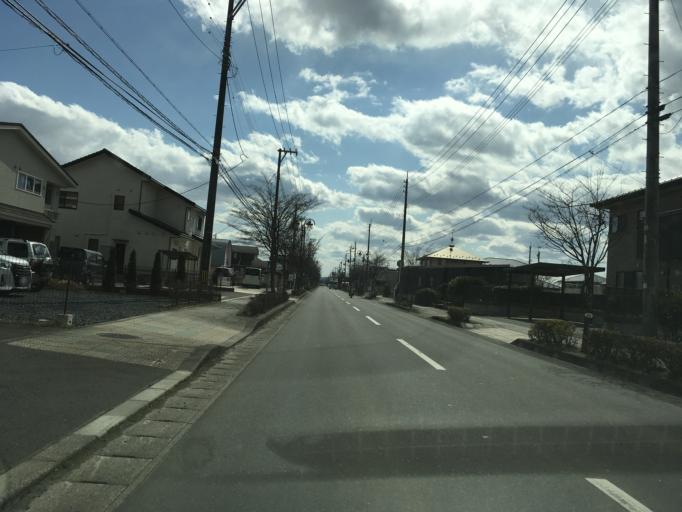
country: JP
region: Miyagi
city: Wakuya
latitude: 38.7057
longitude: 141.2150
